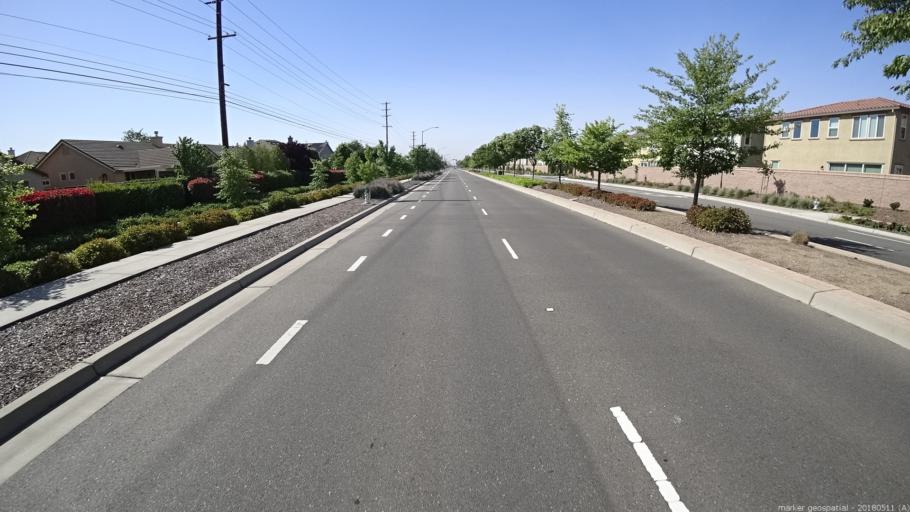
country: US
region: California
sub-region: Yolo County
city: West Sacramento
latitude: 38.6470
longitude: -121.5397
